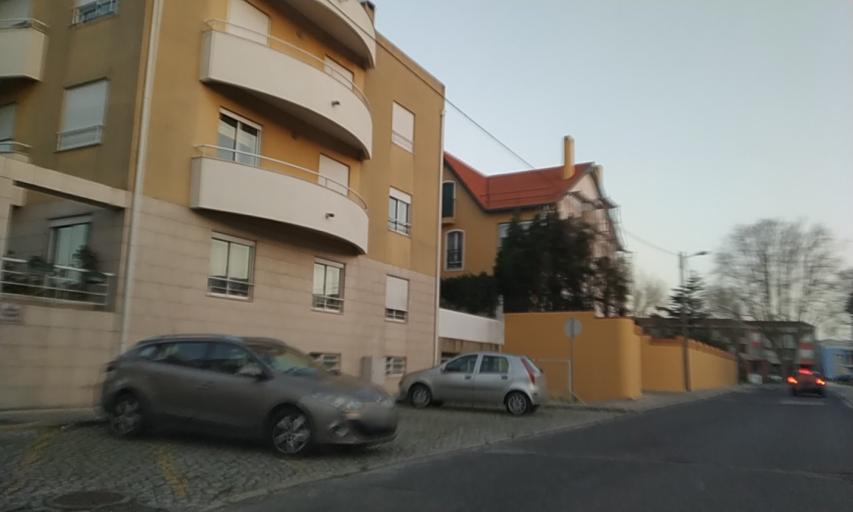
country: PT
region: Leiria
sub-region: Marinha Grande
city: Marinha Grande
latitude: 39.7522
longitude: -8.9292
